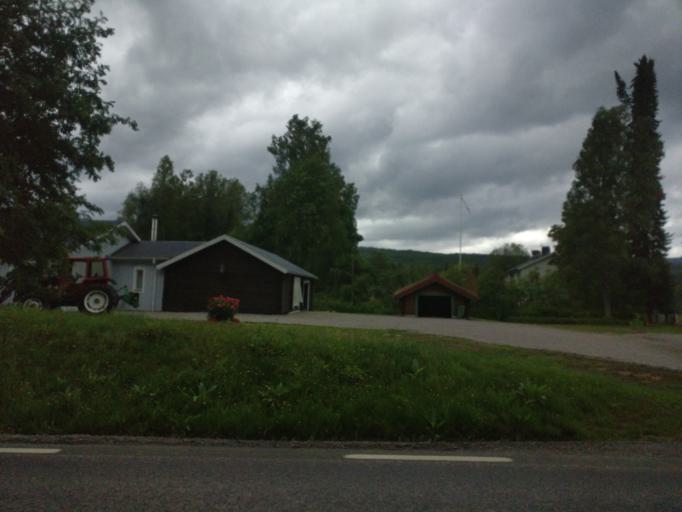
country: SE
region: Vaermland
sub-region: Torsby Kommun
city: Torsby
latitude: 60.6199
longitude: 13.0373
